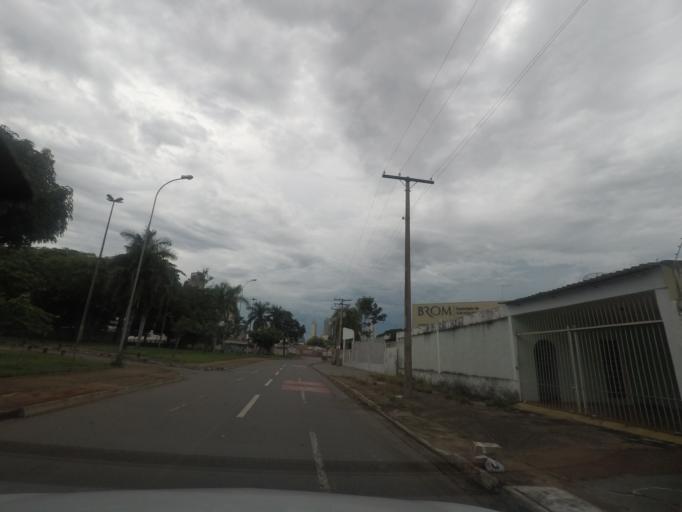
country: BR
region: Goias
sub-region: Goiania
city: Goiania
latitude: -16.6880
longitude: -49.2582
